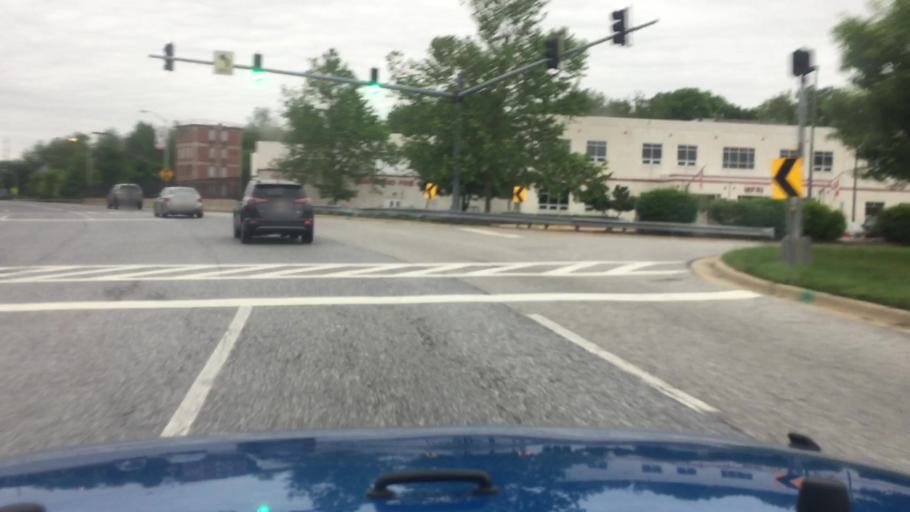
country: US
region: Maryland
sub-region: Prince George's County
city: College Park
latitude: 38.9826
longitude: -76.9283
